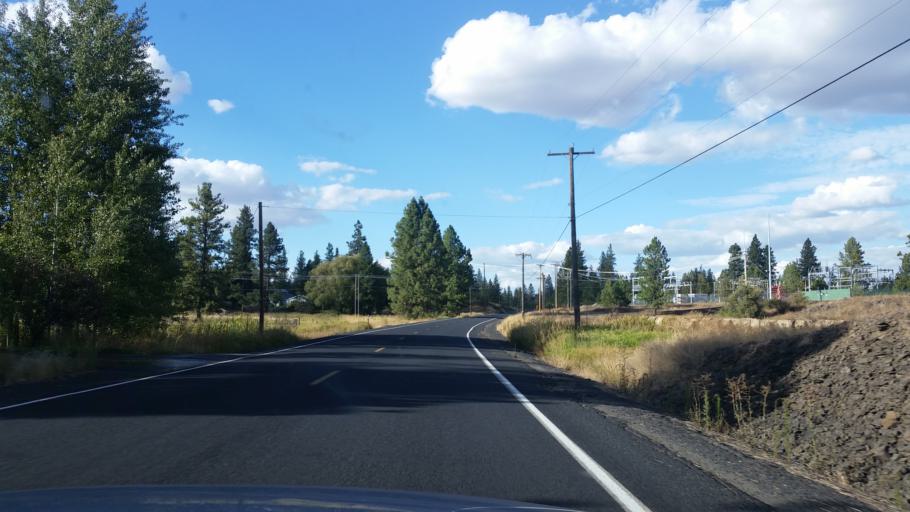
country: US
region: Washington
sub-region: Spokane County
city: Cheney
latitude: 47.4751
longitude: -117.5809
